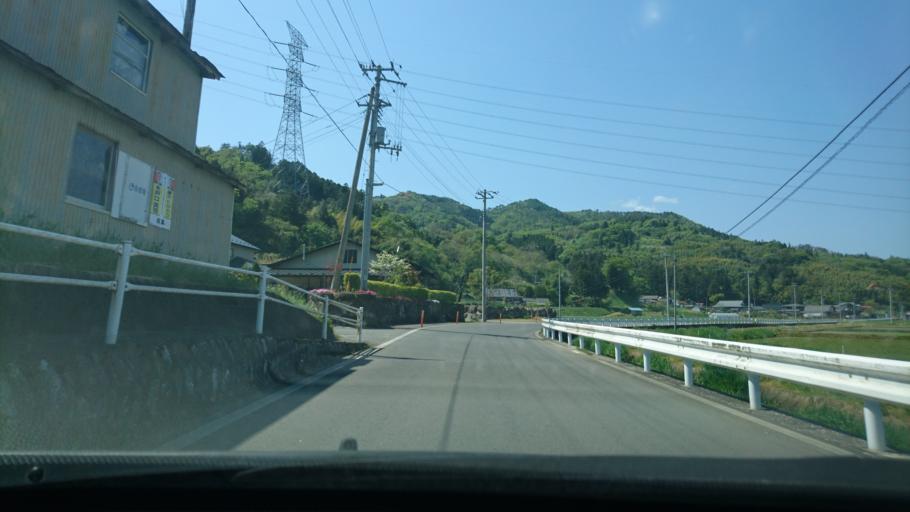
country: JP
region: Iwate
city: Ichinoseki
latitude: 38.9324
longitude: 141.2460
